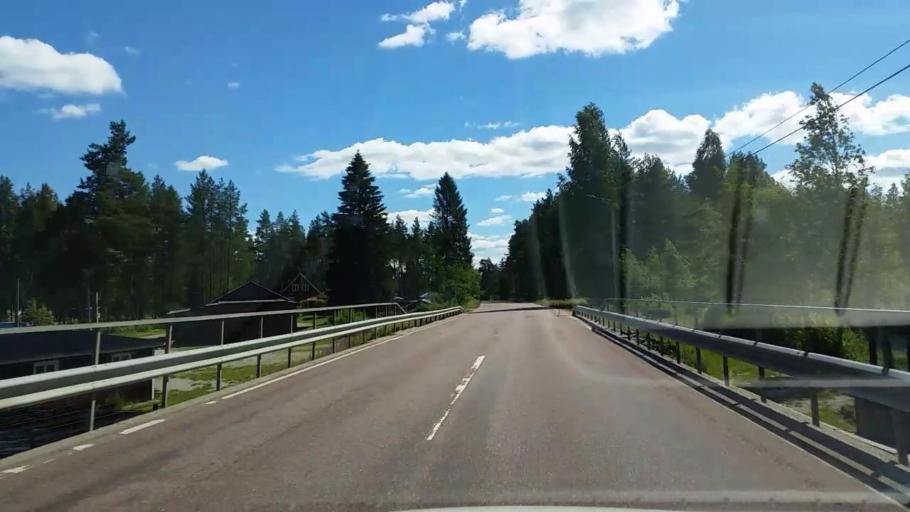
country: SE
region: Dalarna
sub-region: Faluns Kommun
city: Svardsjo
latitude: 60.9868
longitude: 15.7096
